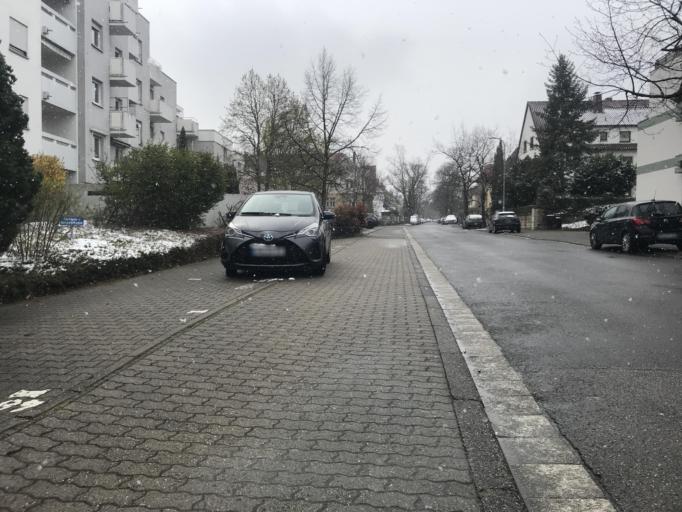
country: DE
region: Rheinland-Pfalz
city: Neustadt
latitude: 49.3482
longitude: 8.1373
